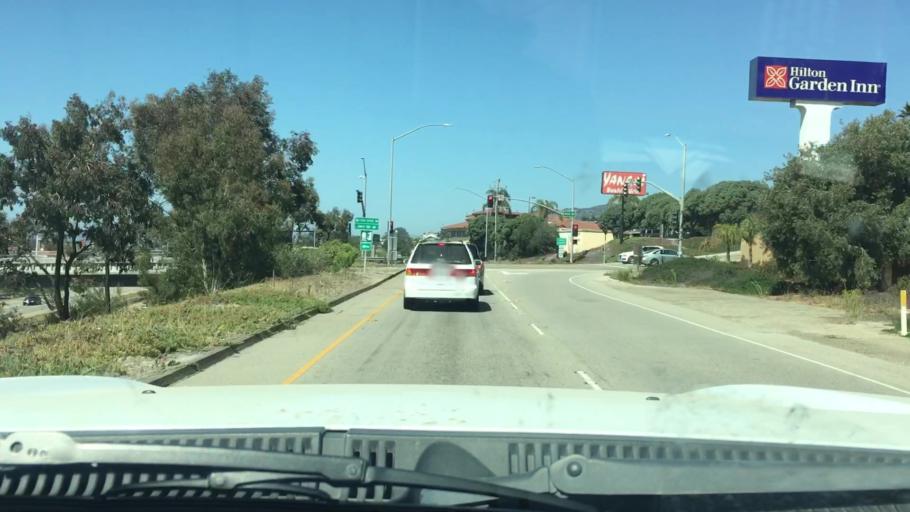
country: US
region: California
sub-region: San Luis Obispo County
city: Grover Beach
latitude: 35.1361
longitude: -120.6207
